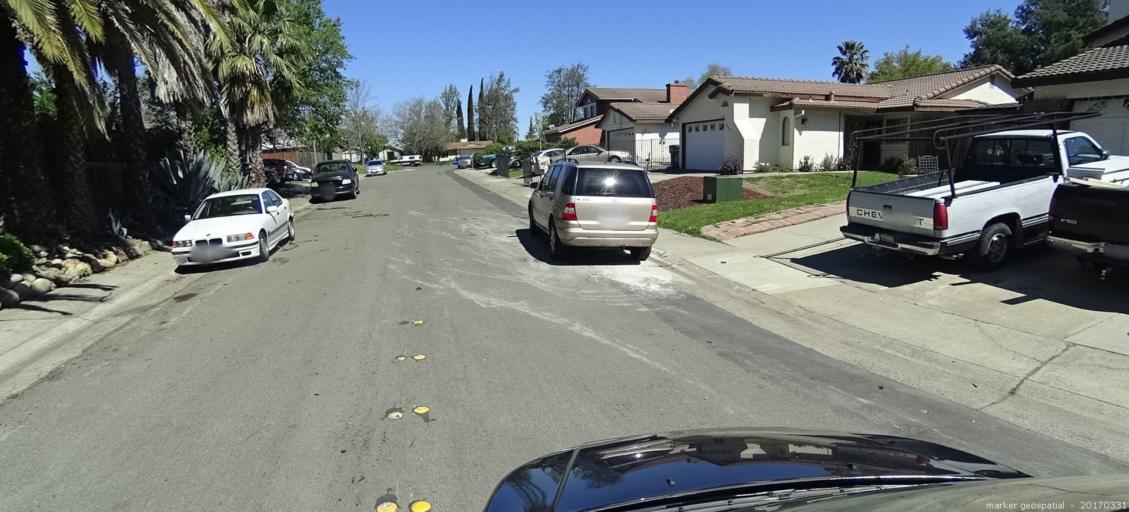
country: US
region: California
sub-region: Sacramento County
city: Parkway
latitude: 38.4645
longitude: -121.4457
